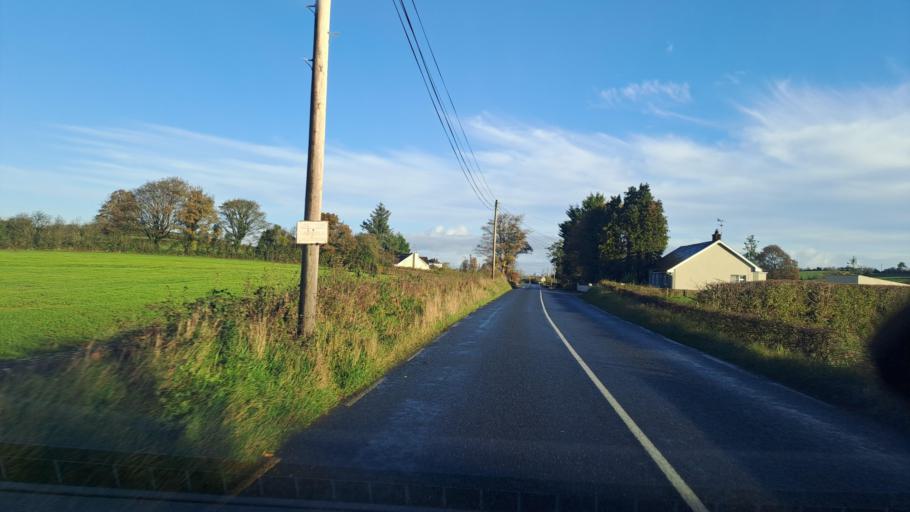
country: IE
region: Ulster
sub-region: County Monaghan
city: Monaghan
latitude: 54.1960
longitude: -6.9898
